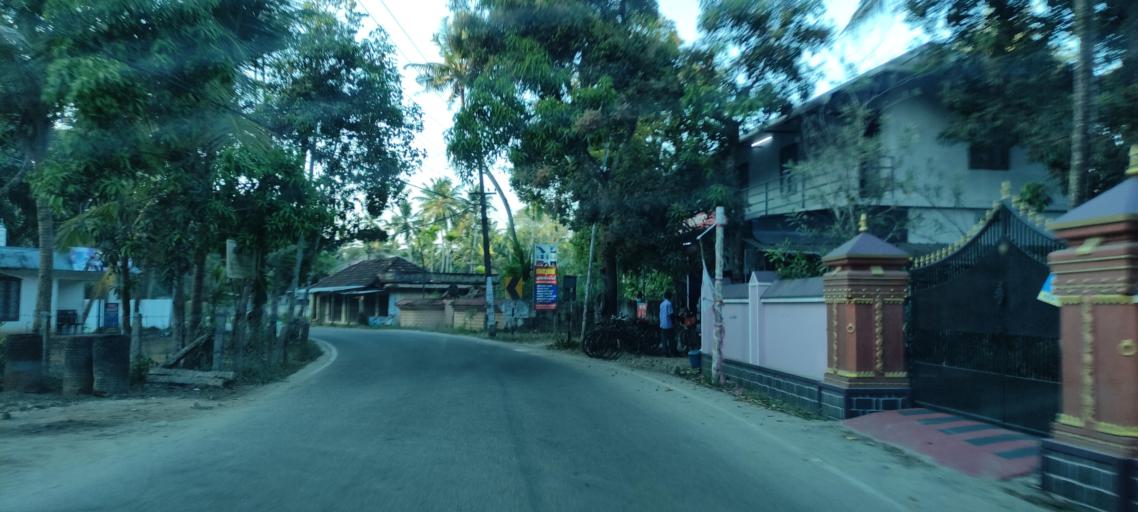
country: IN
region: Kerala
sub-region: Alappuzha
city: Kayankulam
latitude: 9.2023
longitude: 76.4639
